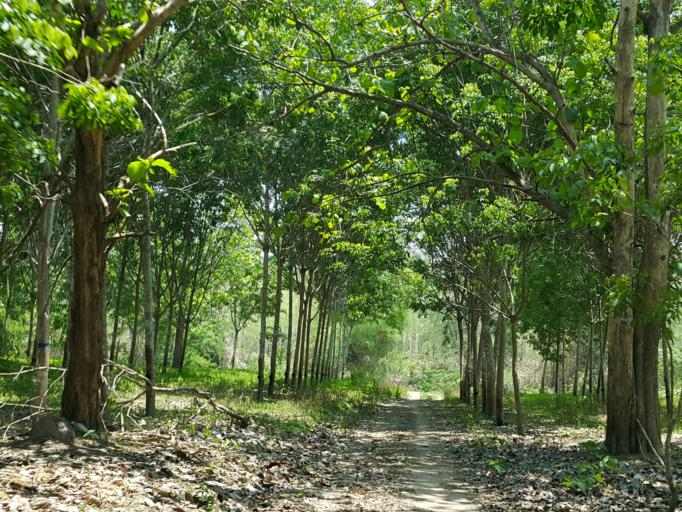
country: TH
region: Kanchanaburi
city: Sai Yok
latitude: 14.2370
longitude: 98.8693
